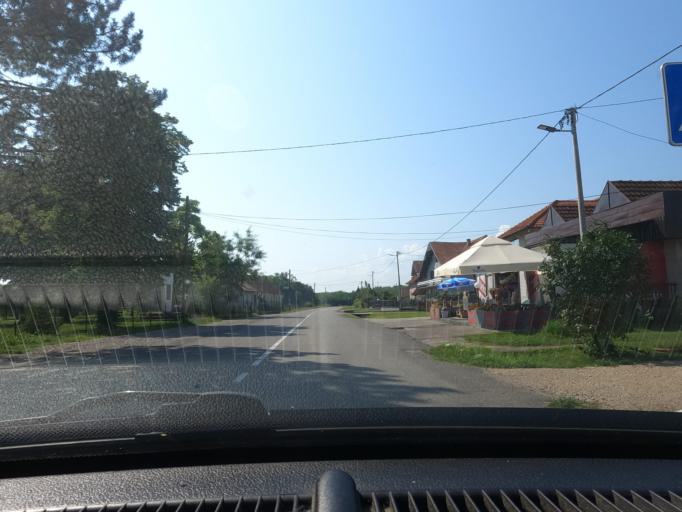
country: RS
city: Kozjak
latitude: 44.5560
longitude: 19.2954
